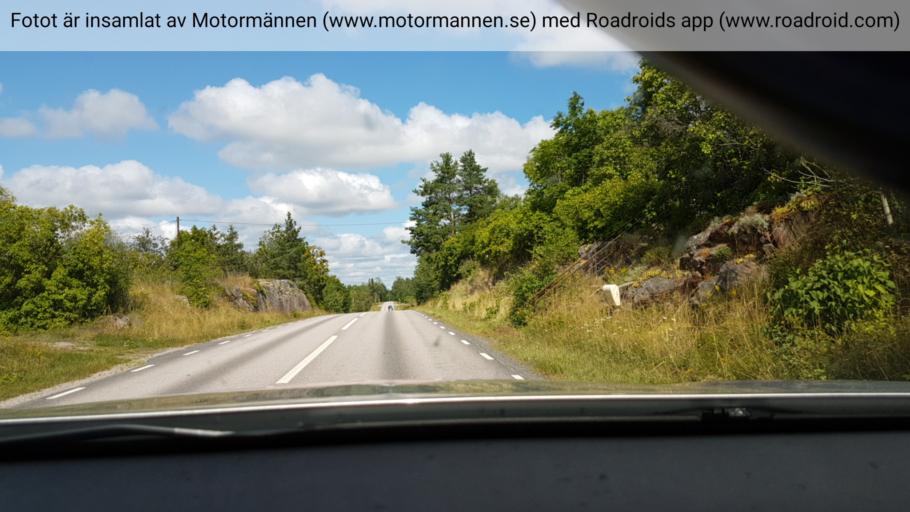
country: SE
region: Stockholm
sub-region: Norrtalje Kommun
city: Arno
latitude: 60.0272
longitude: 18.7880
